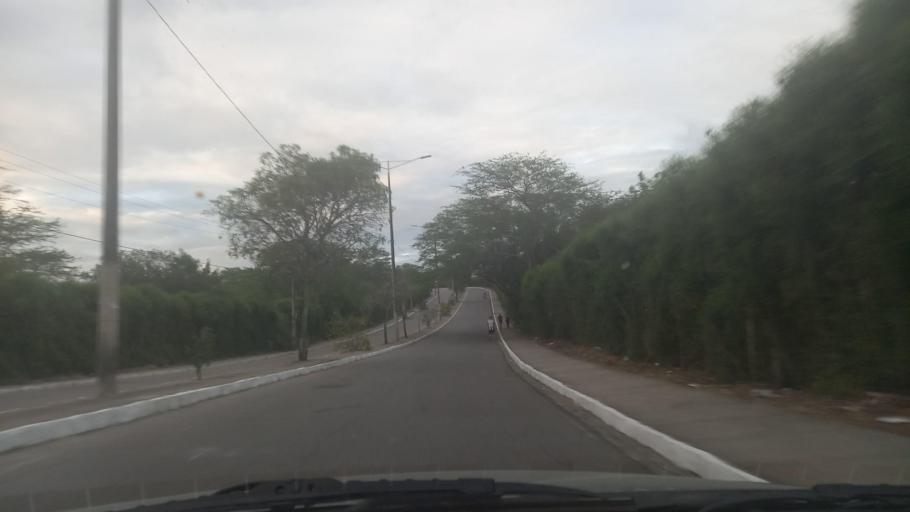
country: BR
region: Pernambuco
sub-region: Caruaru
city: Caruaru
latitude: -8.2597
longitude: -35.9645
